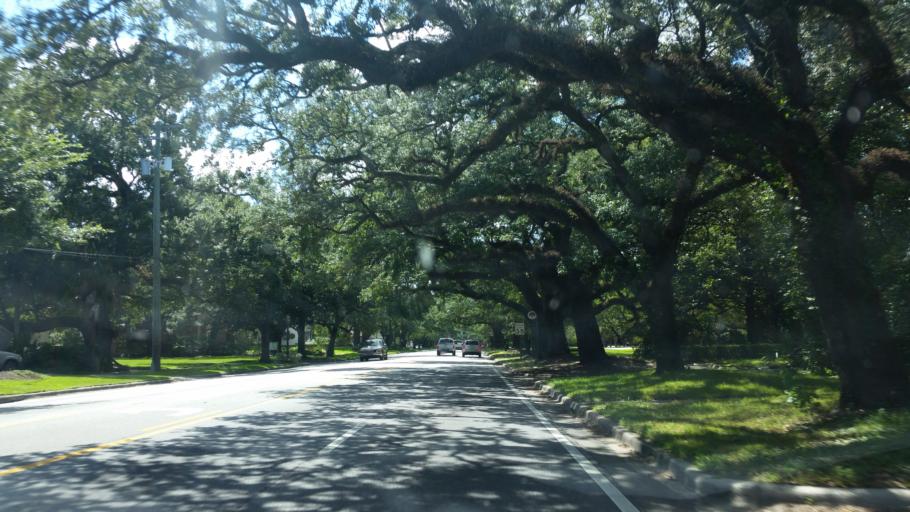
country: US
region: Alabama
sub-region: Mobile County
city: Mobile
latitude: 30.6788
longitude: -88.0783
